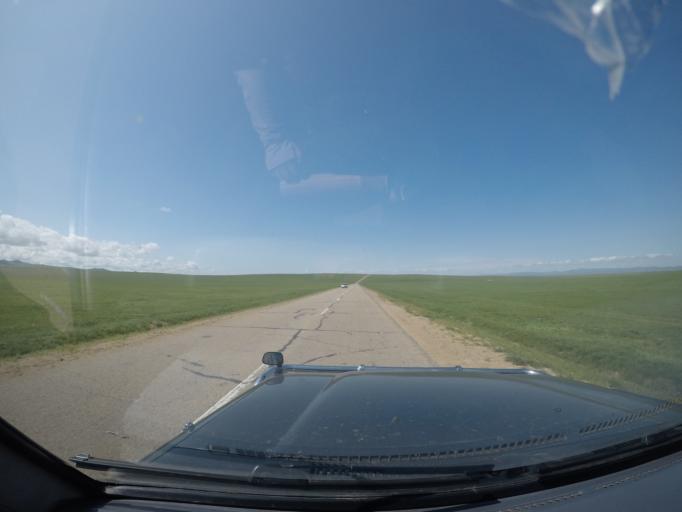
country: MN
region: Hentiy
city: Bayan
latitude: 47.2809
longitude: 110.8869
